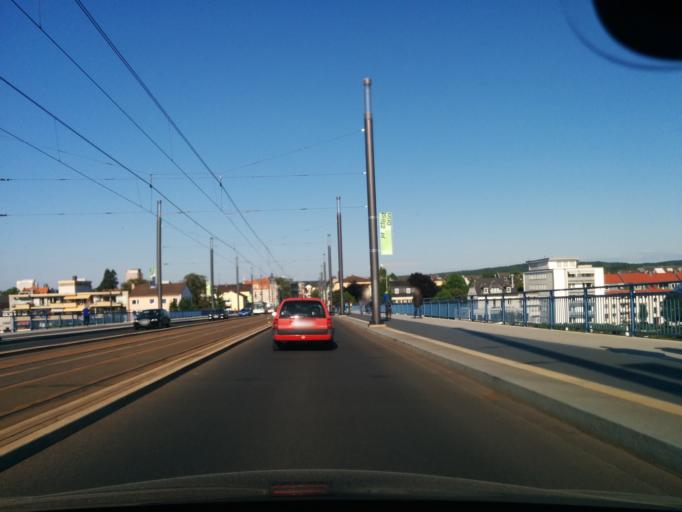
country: DE
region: North Rhine-Westphalia
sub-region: Regierungsbezirk Koln
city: Bonn
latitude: 50.7383
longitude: 7.1113
